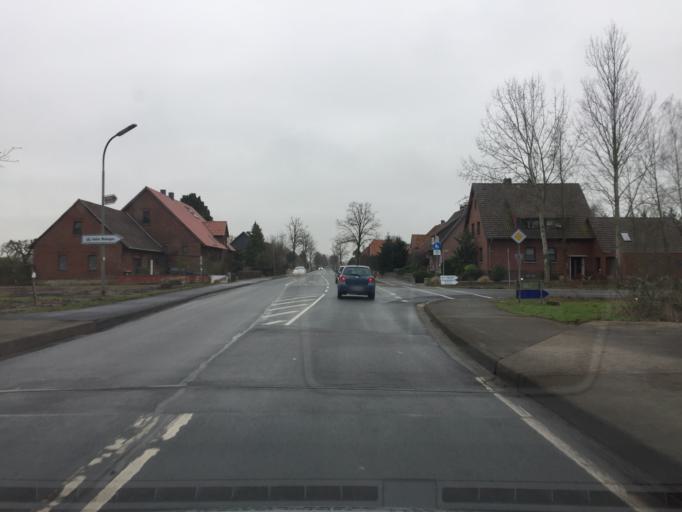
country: DE
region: Lower Saxony
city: Niedernwohren
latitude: 52.3633
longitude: 9.1368
